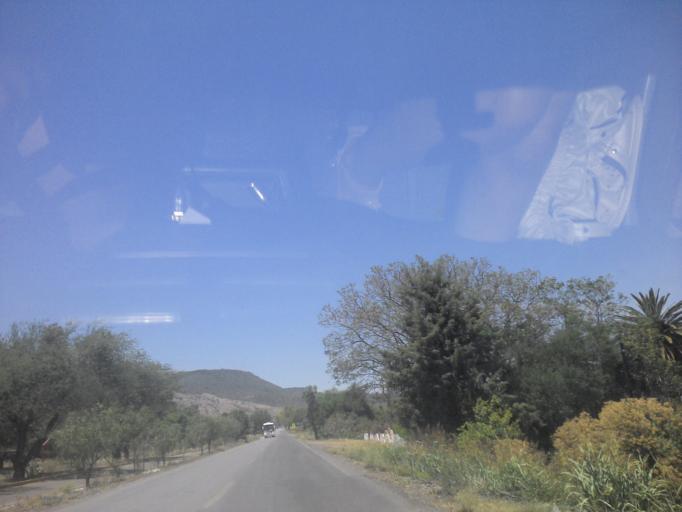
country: MX
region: Guanajuato
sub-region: San Francisco del Rincon
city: San Ignacio de Hidalgo
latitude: 20.9207
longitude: -101.9172
